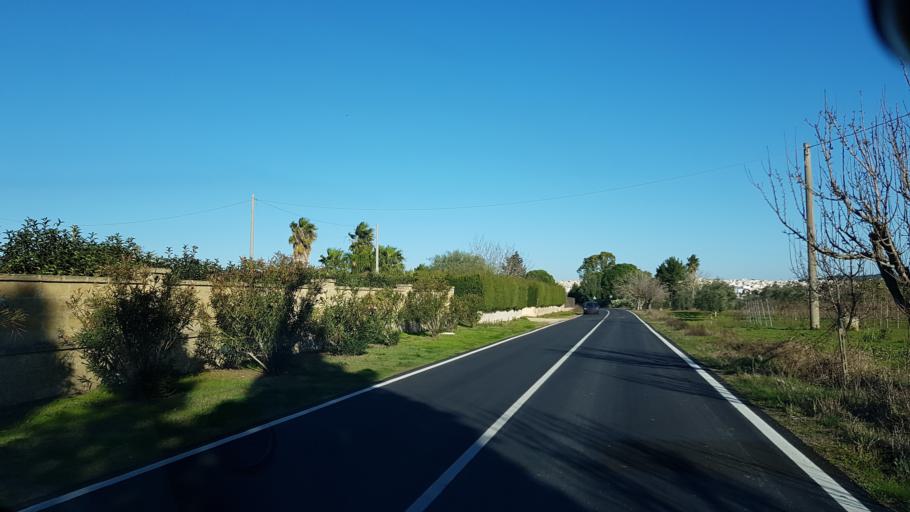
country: IT
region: Apulia
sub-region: Provincia di Lecce
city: Casarano
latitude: 40.0013
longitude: 18.1368
